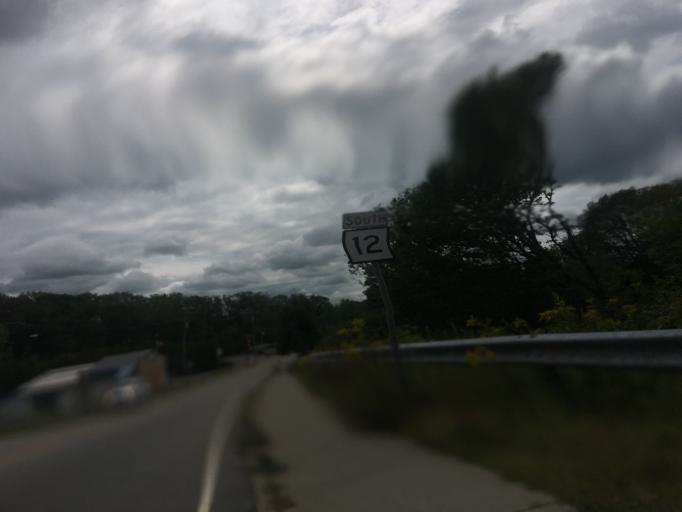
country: US
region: Connecticut
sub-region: Windham County
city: Danielson
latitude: 41.7961
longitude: -71.8848
